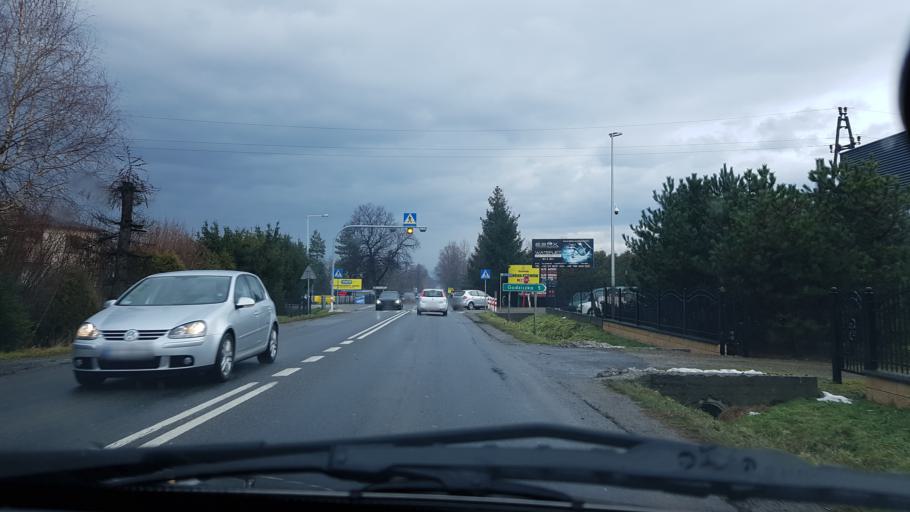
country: PL
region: Silesian Voivodeship
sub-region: Powiat zywiecki
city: Lodygowice
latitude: 49.7242
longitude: 19.1381
